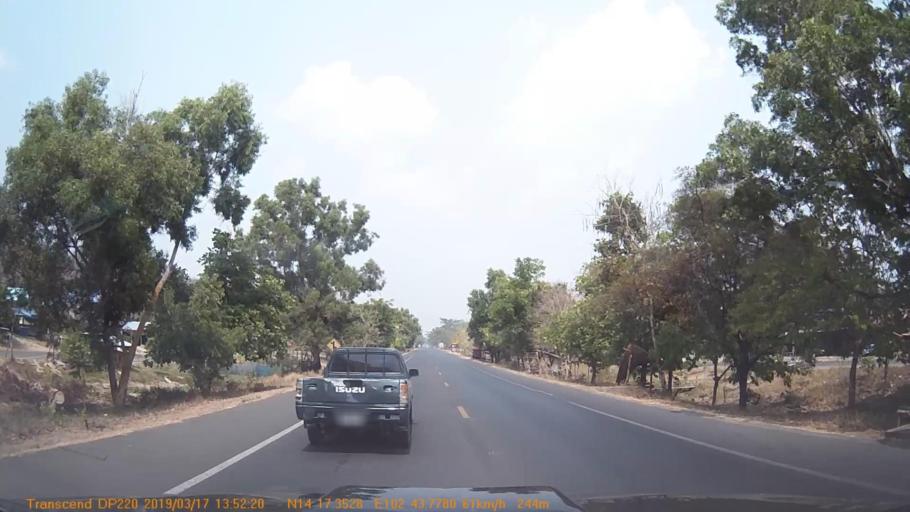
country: TH
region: Buriram
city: Non Din Daeng
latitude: 14.2893
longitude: 102.7298
